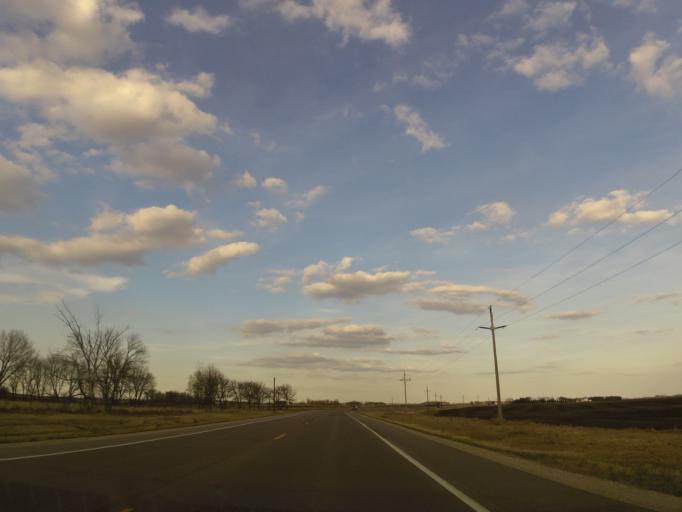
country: US
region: Minnesota
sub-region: McLeod County
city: Hutchinson
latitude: 44.7213
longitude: -94.4764
